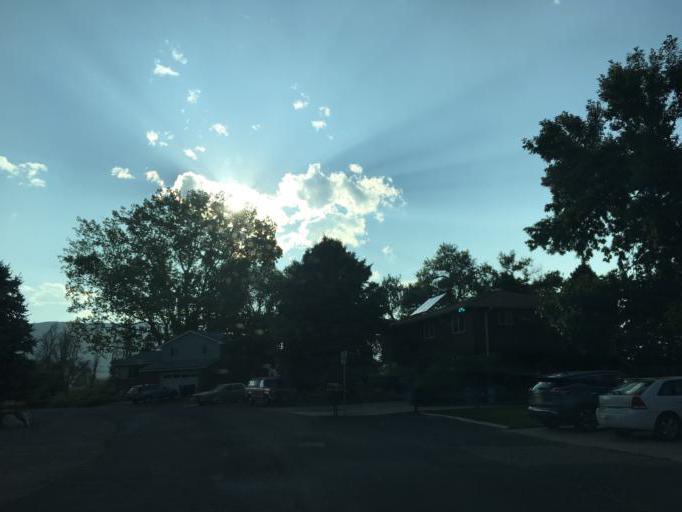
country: US
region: Colorado
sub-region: Jefferson County
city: Applewood
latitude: 39.7945
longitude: -105.1708
